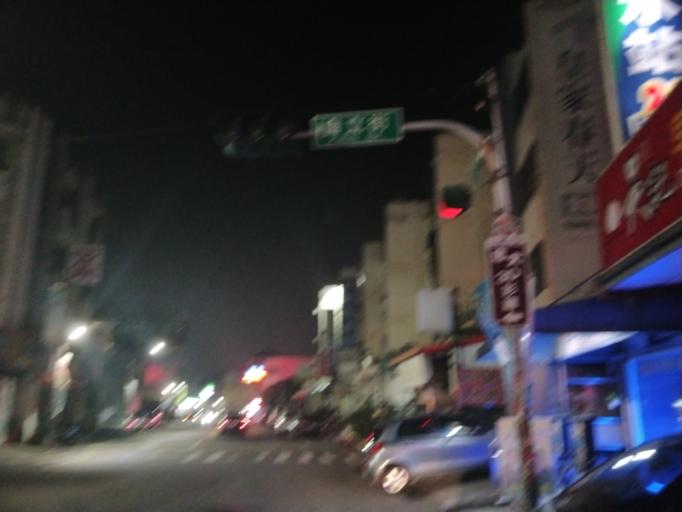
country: TW
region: Taiwan
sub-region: Changhua
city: Chang-hua
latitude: 24.0881
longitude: 120.5362
